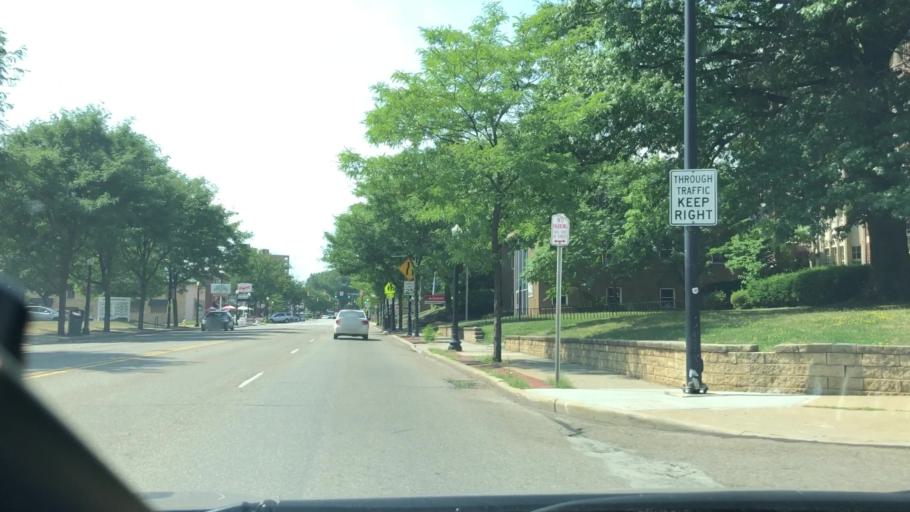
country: US
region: Ohio
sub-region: Summit County
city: Akron
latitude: 41.0956
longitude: -81.5412
